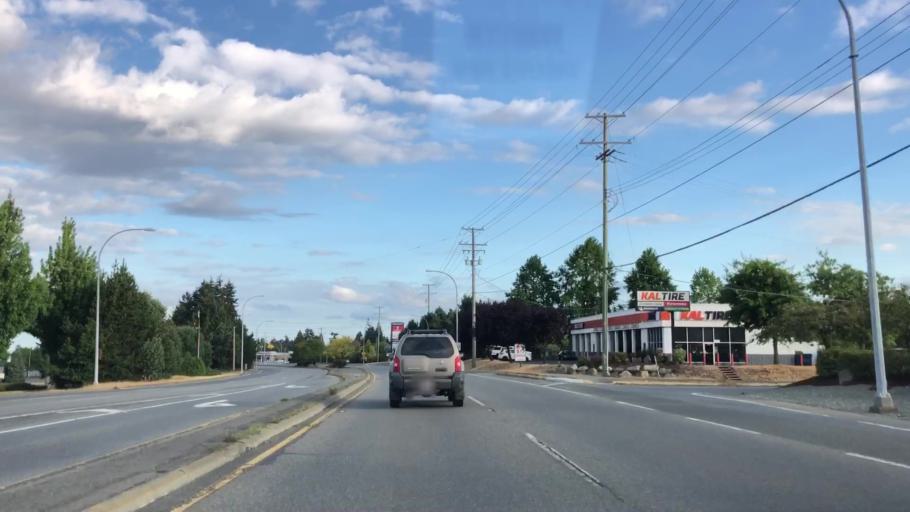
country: CA
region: British Columbia
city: Nanaimo
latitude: 49.2353
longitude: -124.0450
